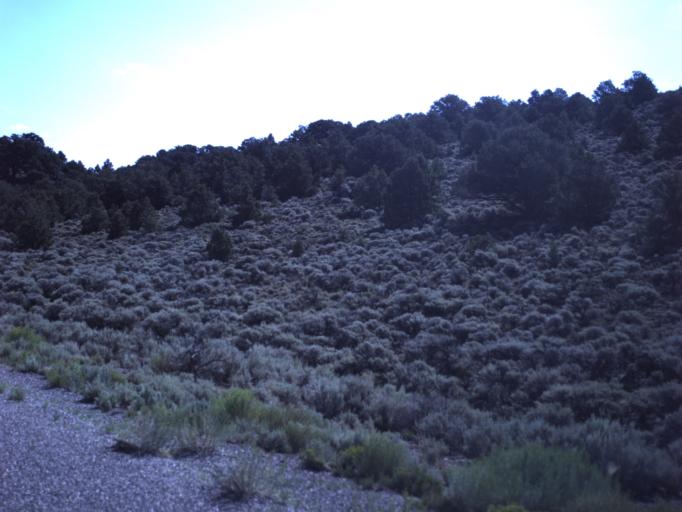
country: US
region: Utah
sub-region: Wayne County
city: Loa
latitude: 38.4842
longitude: -111.5488
